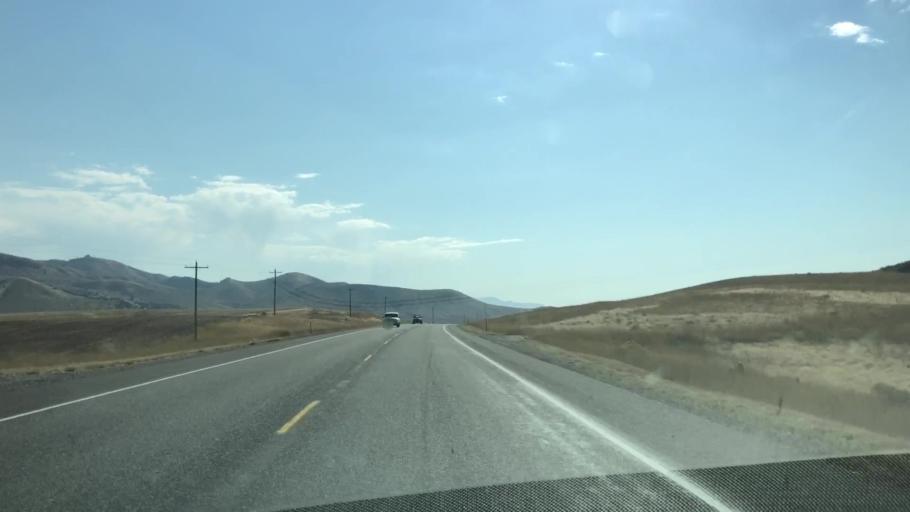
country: US
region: Idaho
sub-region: Madison County
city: Rexburg
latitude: 43.6077
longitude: -111.6683
